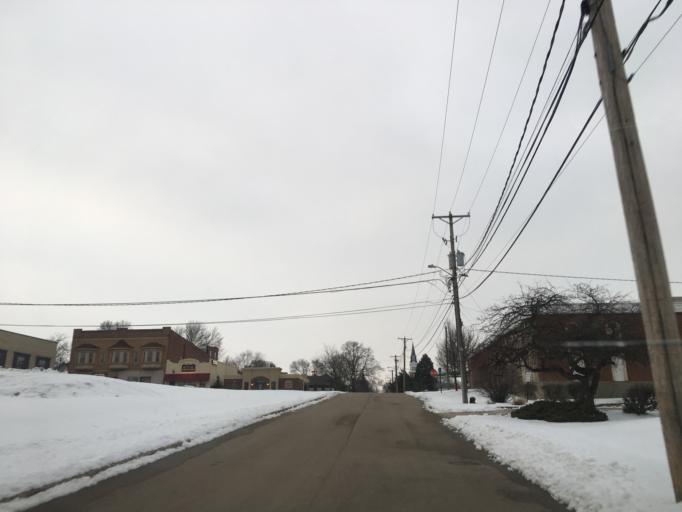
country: US
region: Illinois
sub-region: LaSalle County
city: Peru
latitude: 41.3269
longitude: -89.1265
